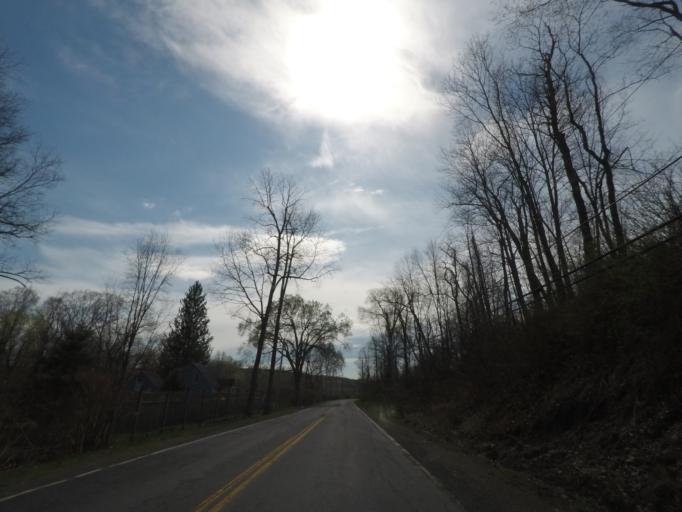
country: US
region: New York
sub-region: Columbia County
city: Chatham
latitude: 42.3515
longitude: -73.5626
